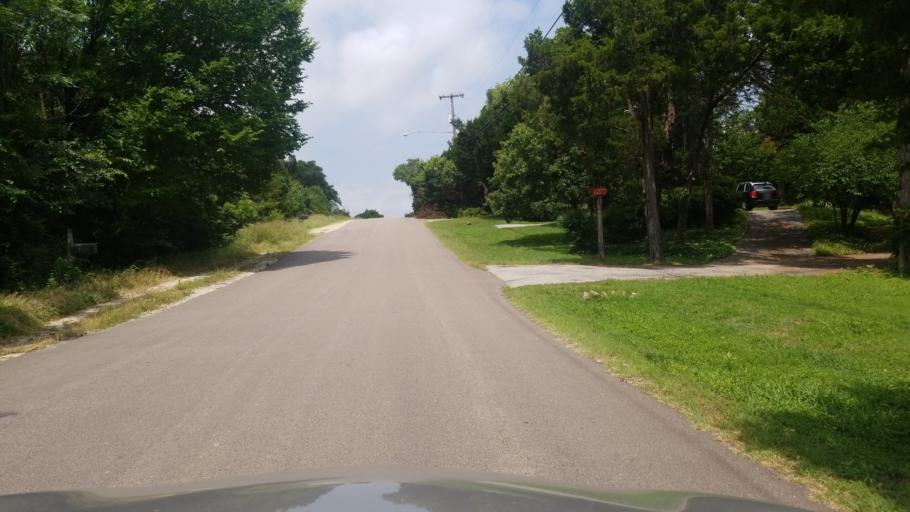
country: US
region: Texas
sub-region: Dallas County
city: Duncanville
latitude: 32.6765
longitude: -96.9282
